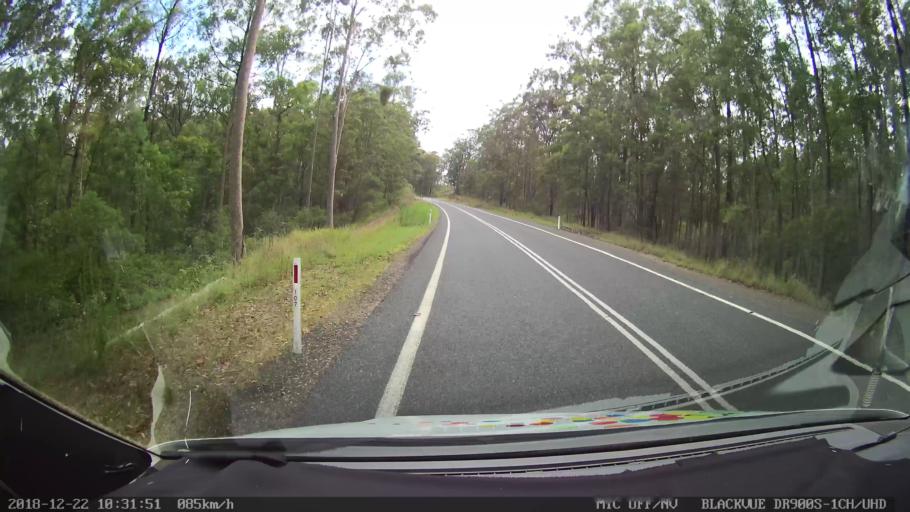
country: AU
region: New South Wales
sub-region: Clarence Valley
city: South Grafton
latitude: -29.6220
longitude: 152.6328
